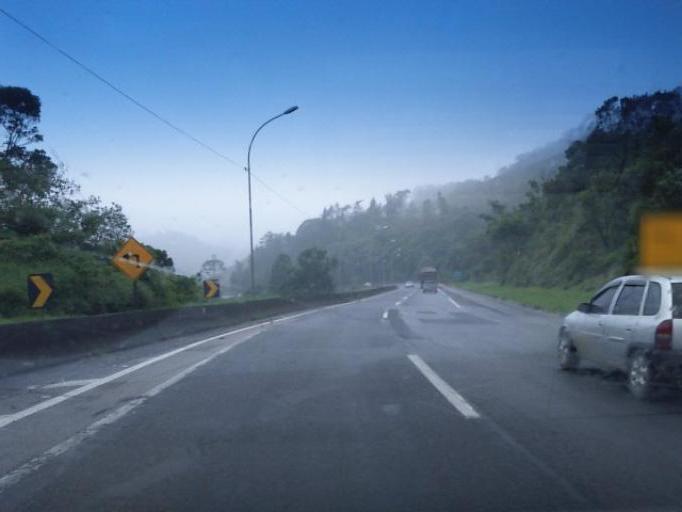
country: BR
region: Parana
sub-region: Campina Grande Do Sul
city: Campina Grande do Sul
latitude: -25.1110
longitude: -48.8063
